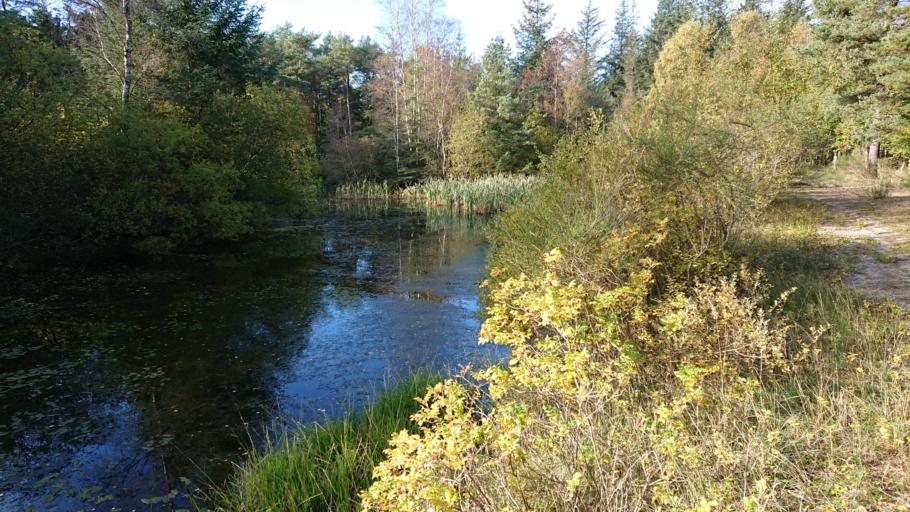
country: DK
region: North Denmark
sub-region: Frederikshavn Kommune
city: Strandby
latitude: 57.6384
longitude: 10.4505
